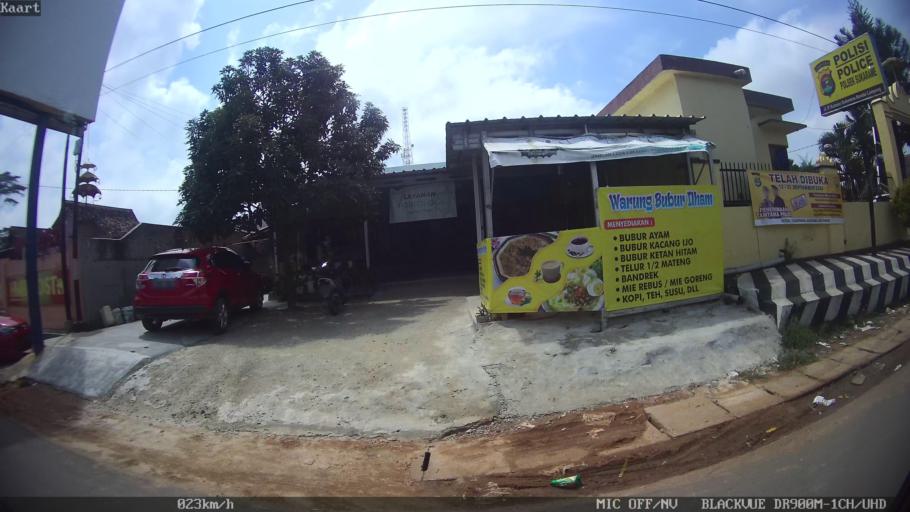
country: ID
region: Lampung
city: Kedaton
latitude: -5.3594
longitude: 105.3054
